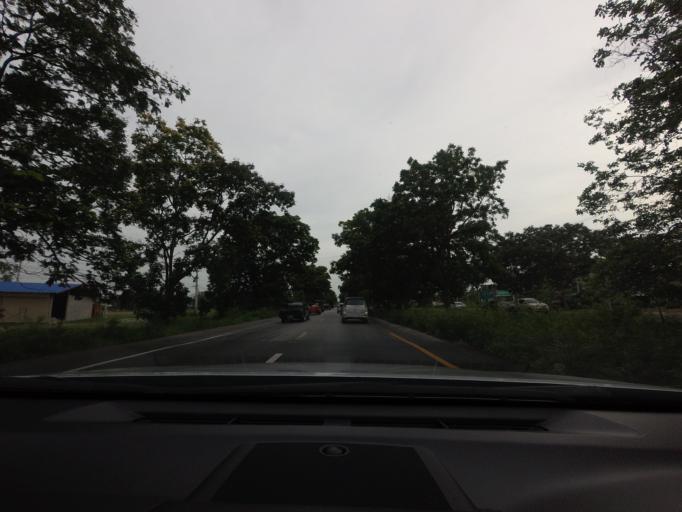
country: TH
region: Phetchaburi
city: Cha-am
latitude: 12.7155
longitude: 99.9180
